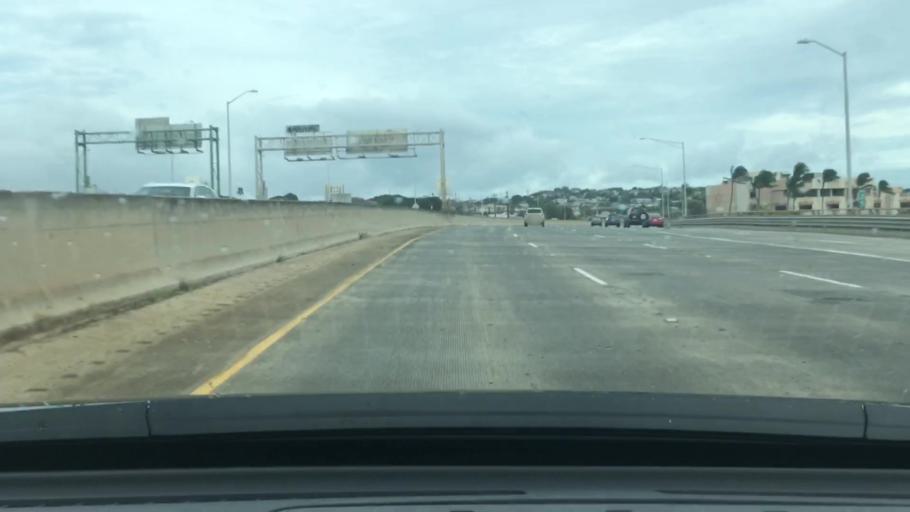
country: US
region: Hawaii
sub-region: Honolulu County
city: Honolulu
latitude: 21.2887
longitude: -157.8142
